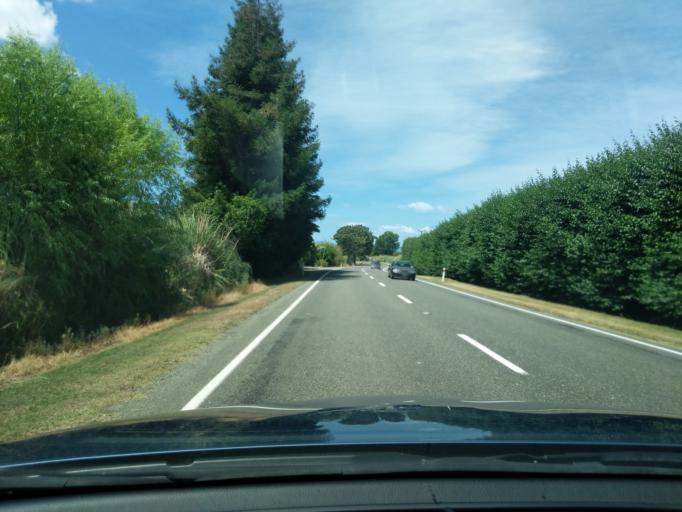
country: NZ
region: Tasman
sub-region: Tasman District
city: Motueka
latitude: -41.0602
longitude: 172.9726
